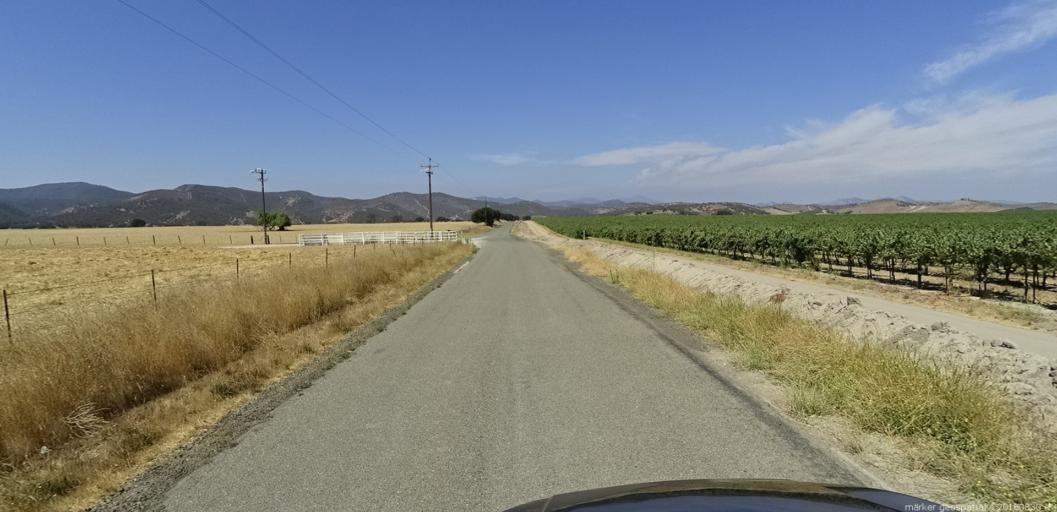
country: US
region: California
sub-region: Monterey County
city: King City
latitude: 36.1109
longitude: -121.0823
